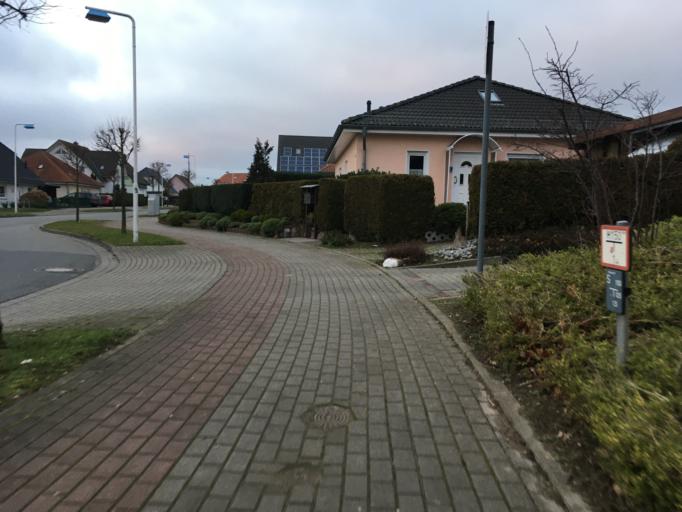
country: DE
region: Mecklenburg-Vorpommern
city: Sassnitz
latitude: 54.5112
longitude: 13.6121
